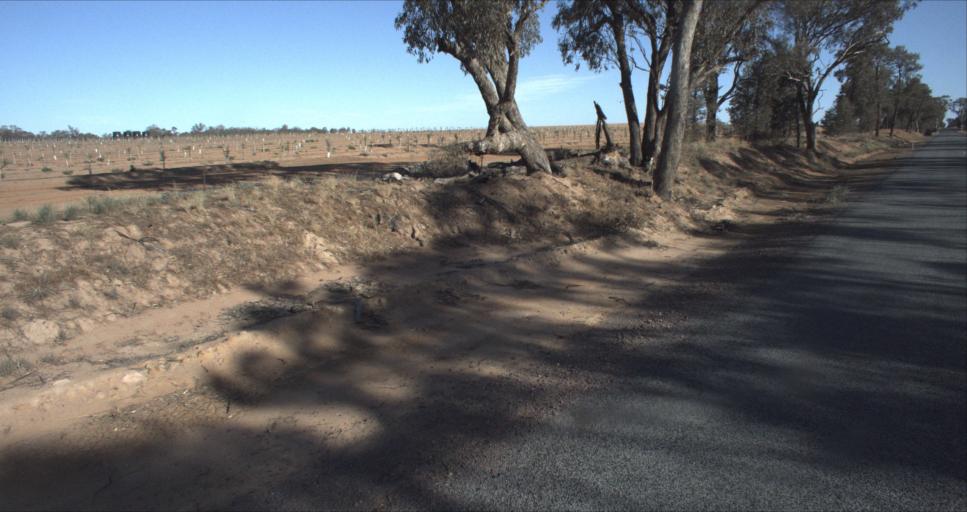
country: AU
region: New South Wales
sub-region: Leeton
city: Leeton
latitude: -34.6504
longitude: 146.3514
